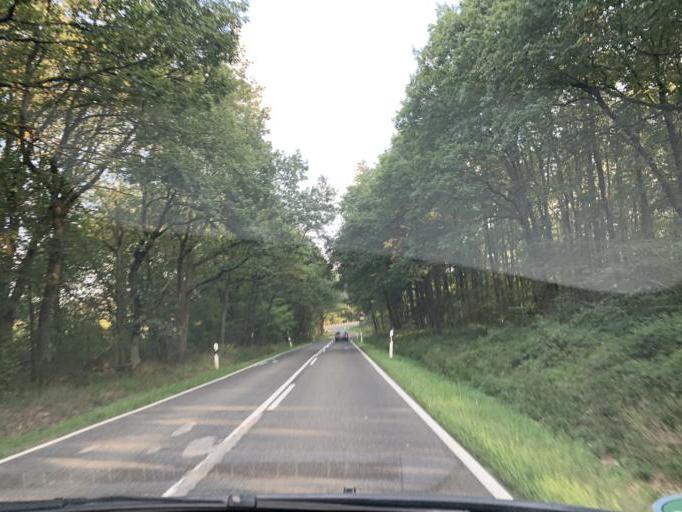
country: DE
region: North Rhine-Westphalia
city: Heimbach
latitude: 50.6494
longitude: 6.4502
